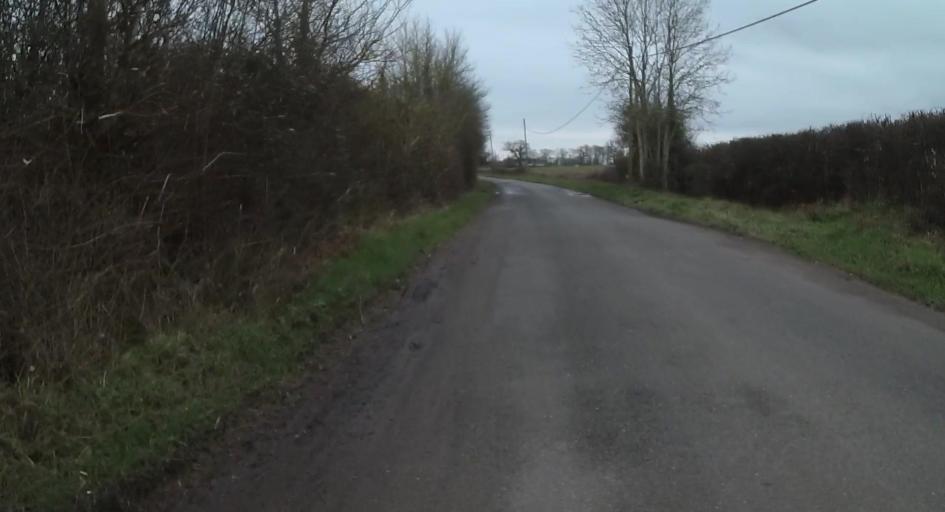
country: GB
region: England
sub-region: West Berkshire
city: Stratfield Mortimer
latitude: 51.3834
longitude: -1.0393
